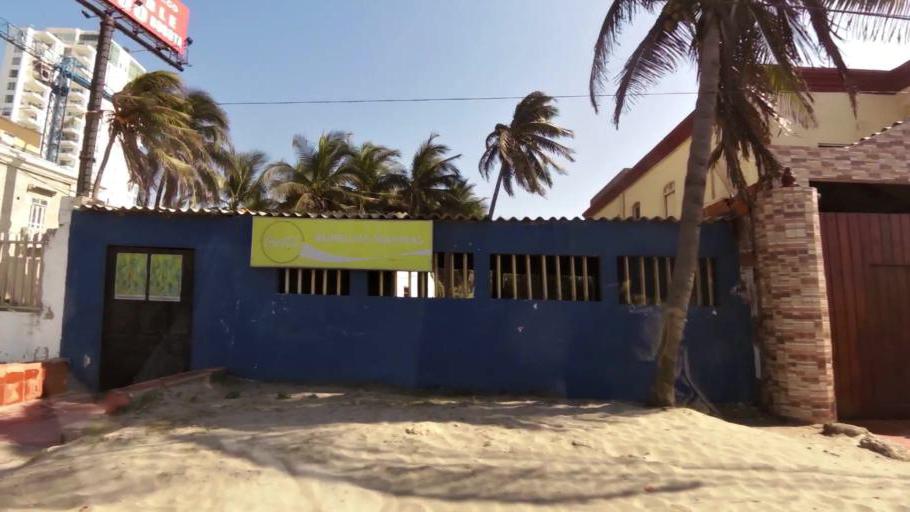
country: CO
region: Bolivar
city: Cartagena
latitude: 10.4323
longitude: -75.5438
